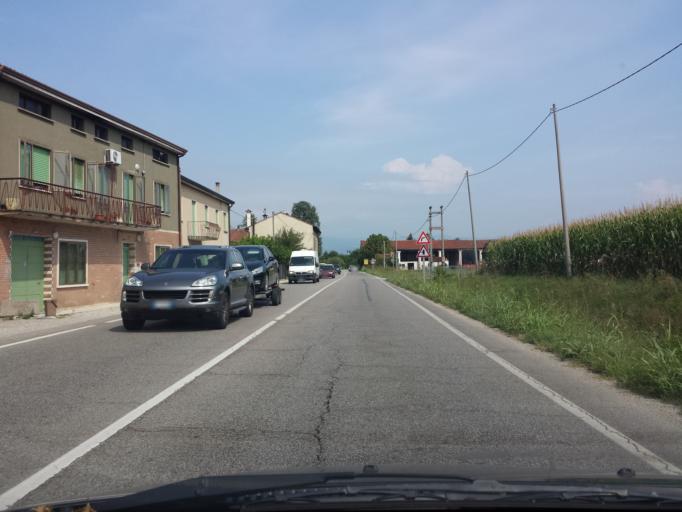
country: IT
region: Veneto
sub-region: Provincia di Vicenza
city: Monticello Conte Otto
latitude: 45.6040
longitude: 11.5554
